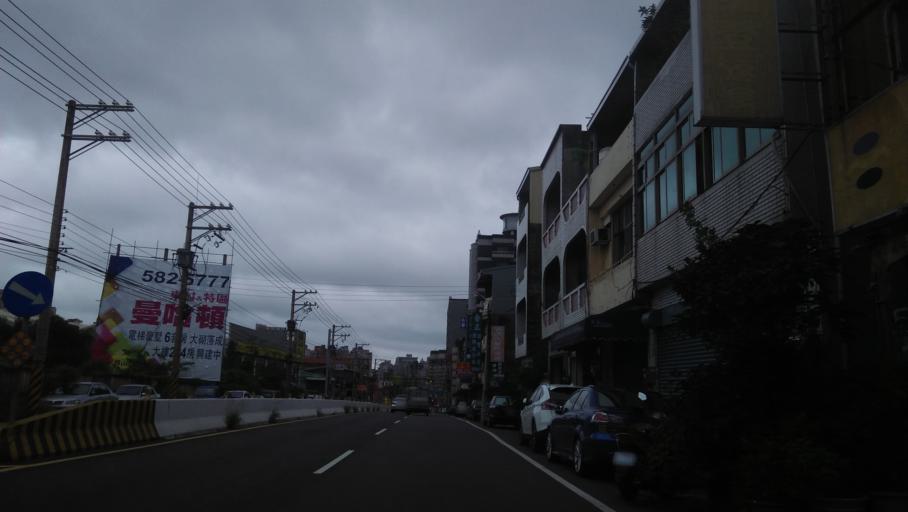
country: TW
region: Taiwan
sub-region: Hsinchu
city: Zhubei
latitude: 24.7789
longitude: 121.0308
